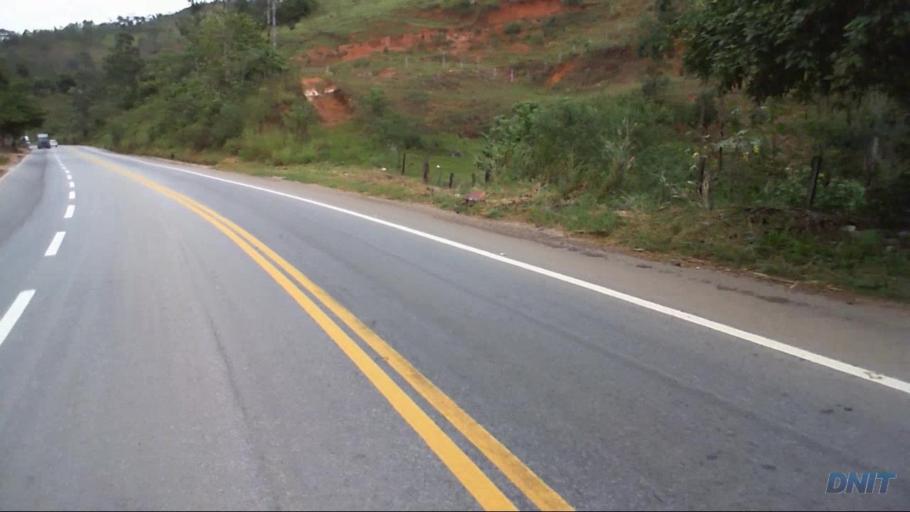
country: BR
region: Minas Gerais
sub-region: Timoteo
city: Timoteo
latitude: -19.6332
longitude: -42.8330
